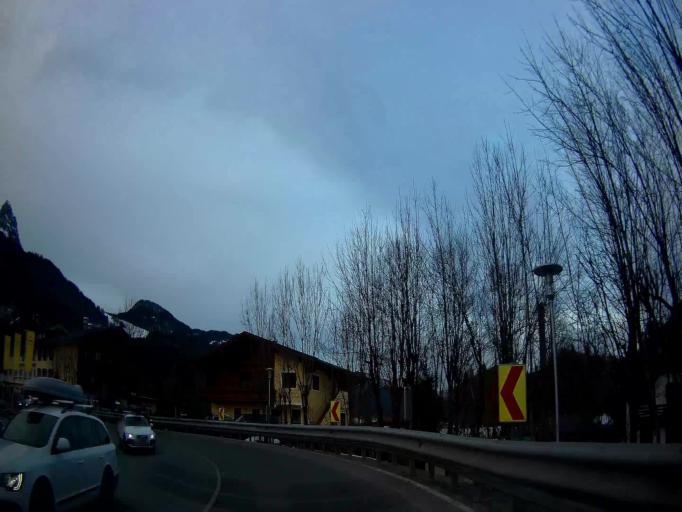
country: AT
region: Salzburg
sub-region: Politischer Bezirk Zell am See
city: Lofer
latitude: 47.5943
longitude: 12.6997
